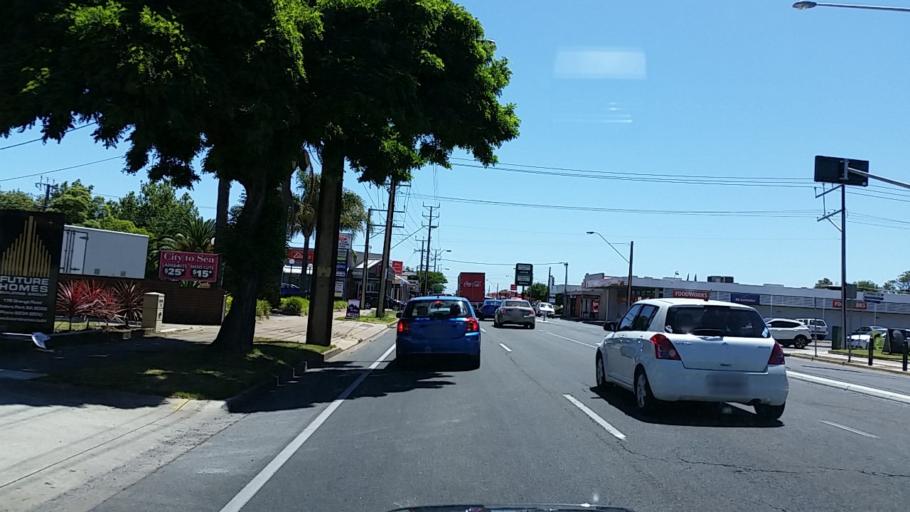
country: AU
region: South Australia
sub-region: Charles Sturt
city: Allenby Gardens
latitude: -34.9047
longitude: 138.5483
